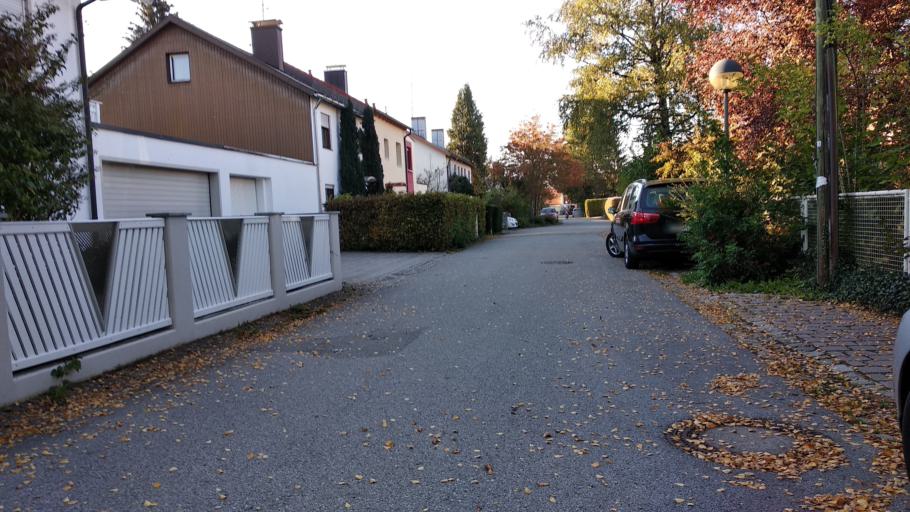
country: DE
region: Bavaria
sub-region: Upper Bavaria
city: Vaterstetten
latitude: 48.1060
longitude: 11.7666
